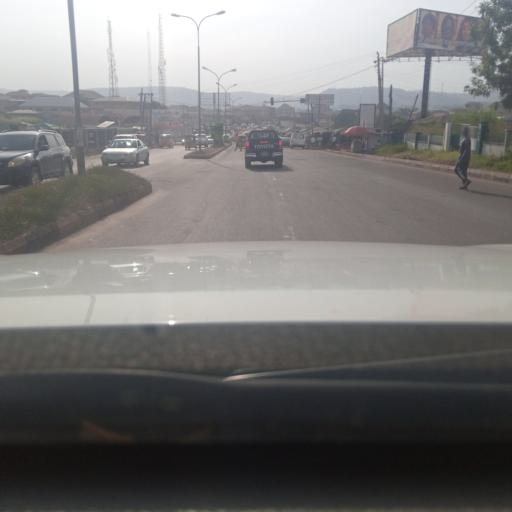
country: NG
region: Enugu
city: Enugu
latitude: 6.4410
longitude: 7.5080
